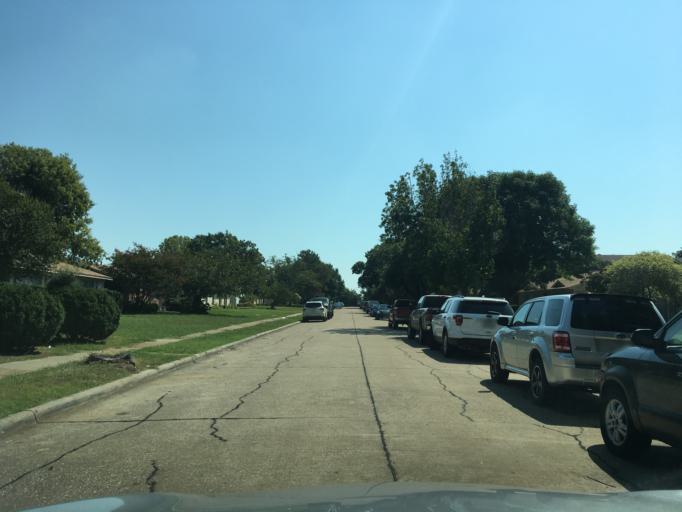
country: US
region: Texas
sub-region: Dallas County
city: Garland
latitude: 32.9322
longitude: -96.6559
